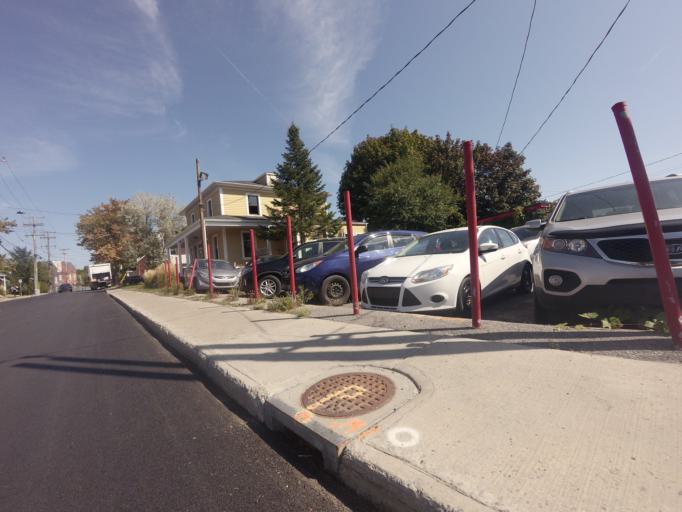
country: CA
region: Quebec
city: Kirkland
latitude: 45.4834
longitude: -73.8673
